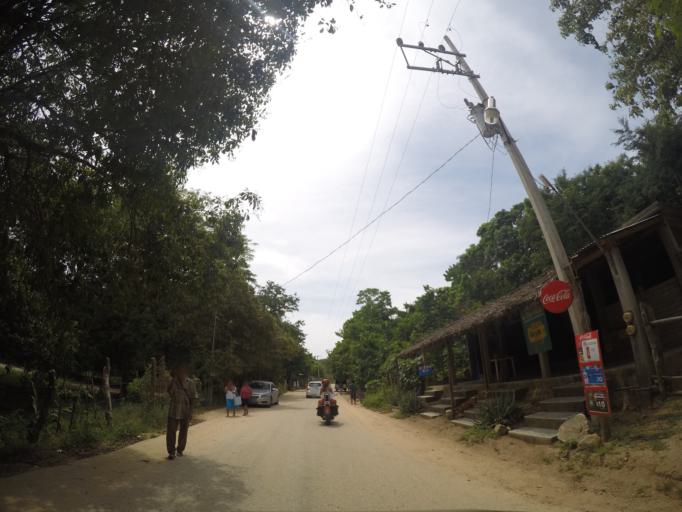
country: MX
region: Oaxaca
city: Santa Maria Tonameca
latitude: 15.6668
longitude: -96.5214
